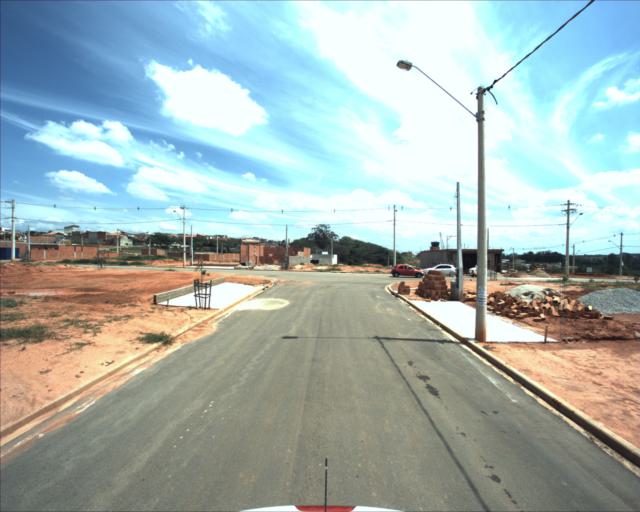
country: BR
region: Sao Paulo
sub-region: Sorocaba
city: Sorocaba
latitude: -23.4085
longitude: -47.4070
